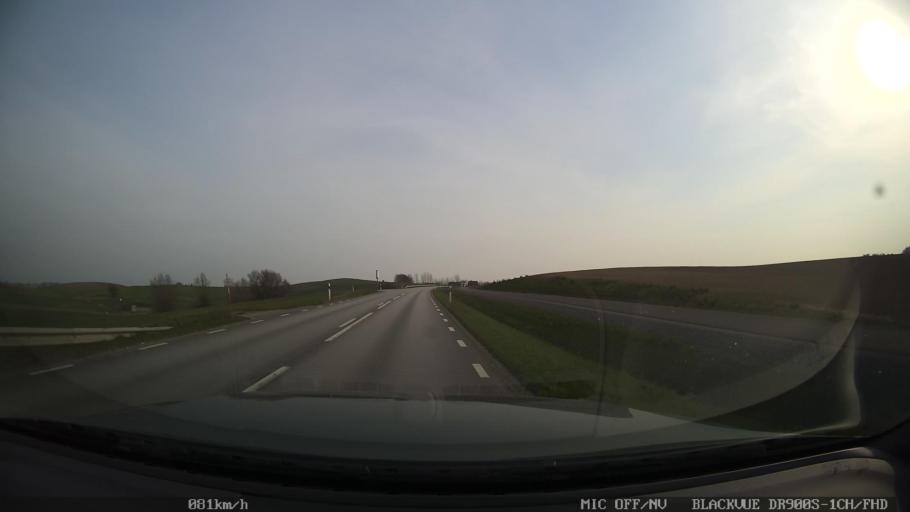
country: SE
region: Skane
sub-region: Ystads Kommun
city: Ystad
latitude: 55.4653
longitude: 13.7989
